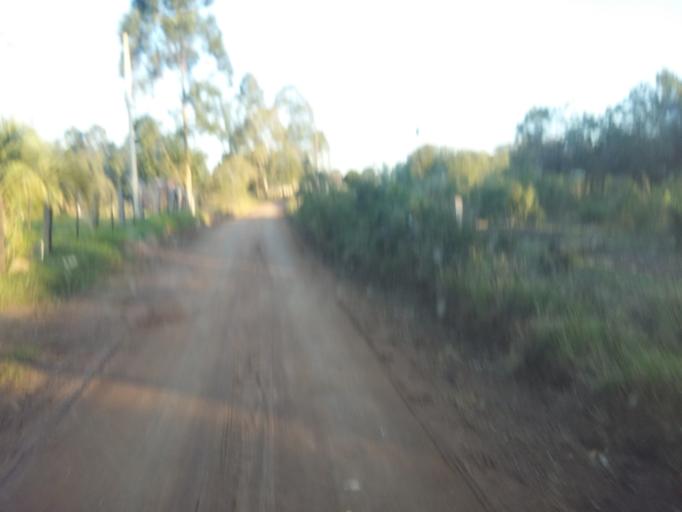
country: BR
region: Rio Grande do Sul
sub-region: Camaqua
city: Camaqua
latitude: -30.7155
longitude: -51.7699
